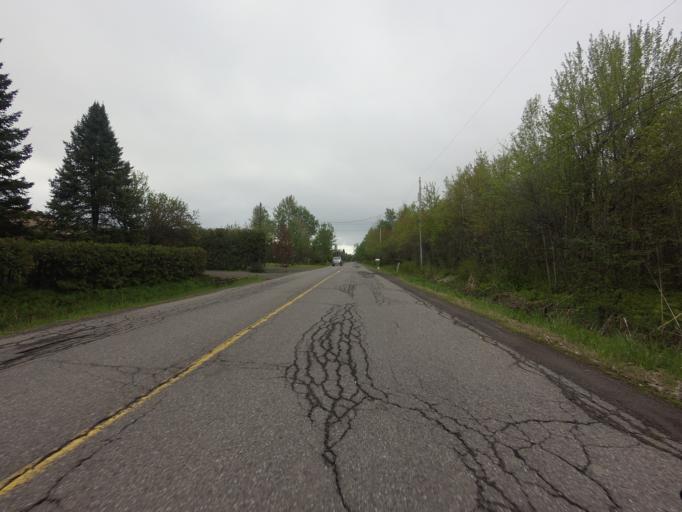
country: CA
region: Ontario
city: Ottawa
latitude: 45.3578
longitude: -75.5053
